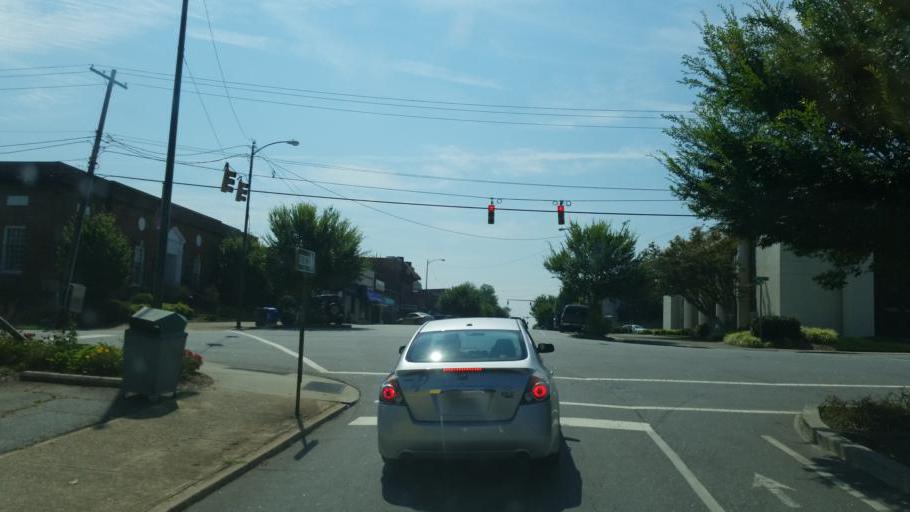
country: US
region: North Carolina
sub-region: Burke County
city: Morganton
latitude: 35.7471
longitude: -81.6903
